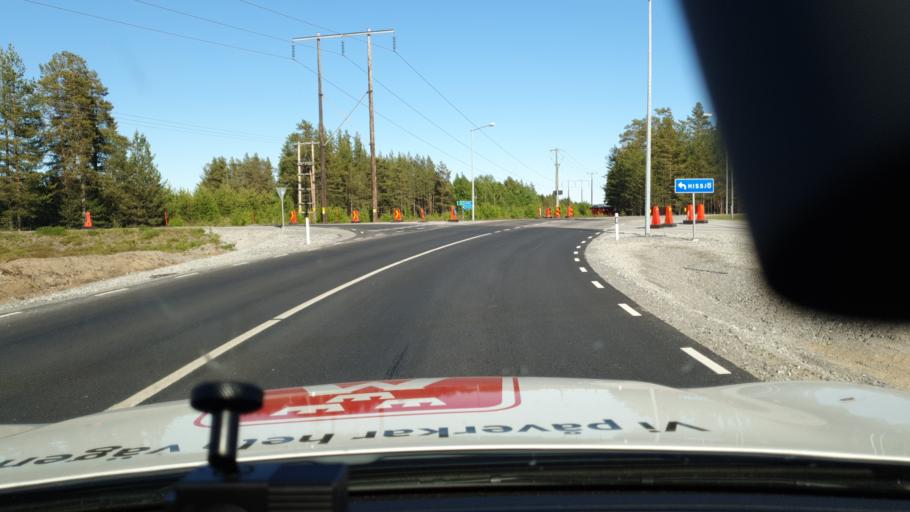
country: SE
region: Vaesterbotten
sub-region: Umea Kommun
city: Roback
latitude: 63.8483
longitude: 20.1560
